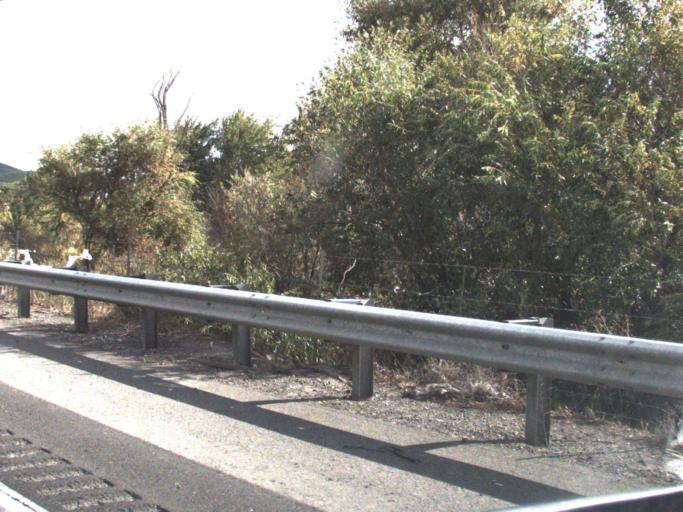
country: US
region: Washington
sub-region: Yakima County
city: Union Gap
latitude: 46.5201
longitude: -120.4635
